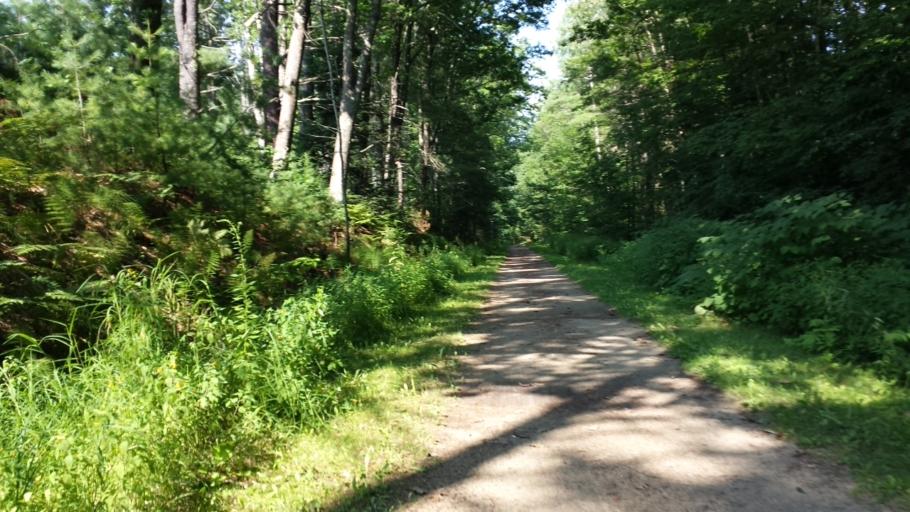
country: US
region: Maine
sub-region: York County
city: Kennebunk
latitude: 43.4347
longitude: -70.5304
